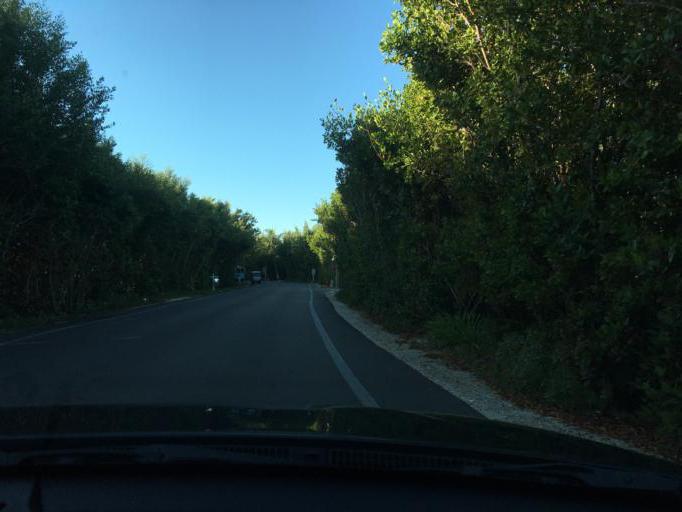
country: US
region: Florida
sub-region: Lee County
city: Pine Island Center
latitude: 26.5362
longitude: -82.1941
